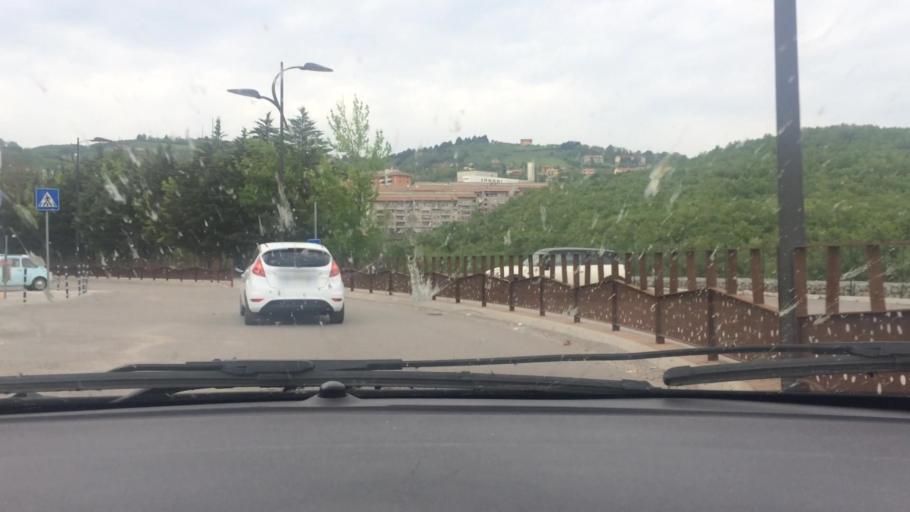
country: IT
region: Basilicate
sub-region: Provincia di Potenza
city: Potenza
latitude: 40.6529
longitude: 15.8070
